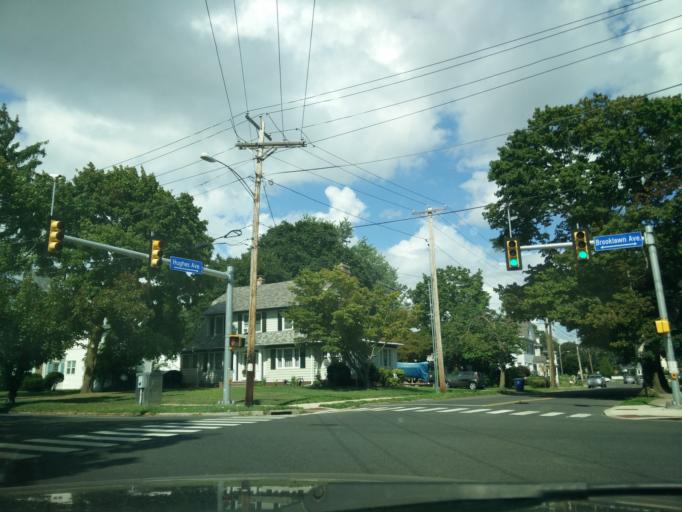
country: US
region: Connecticut
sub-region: Fairfield County
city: Bridgeport
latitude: 41.1832
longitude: -73.2181
